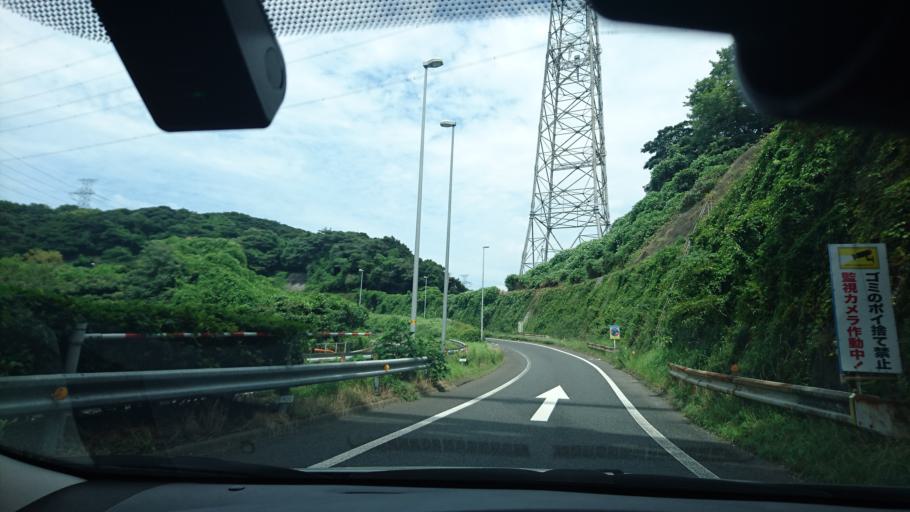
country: JP
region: Yamaguchi
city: Shimonoseki
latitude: 33.9642
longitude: 130.9543
